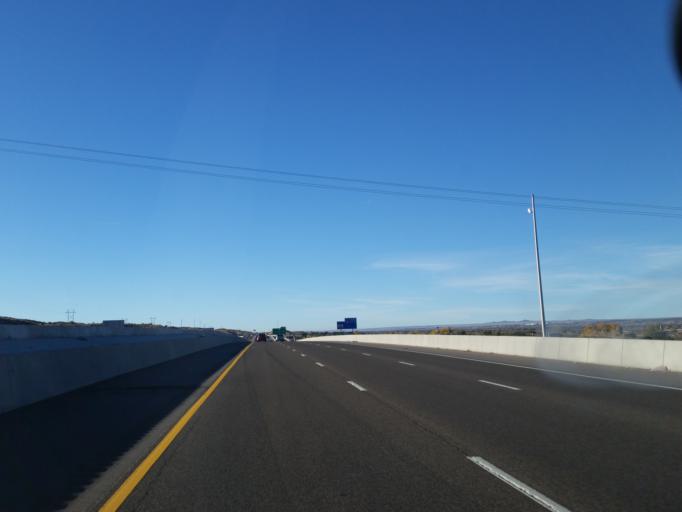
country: US
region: New Mexico
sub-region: Sandoval County
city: Bernalillo
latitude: 35.3035
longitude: -106.5374
